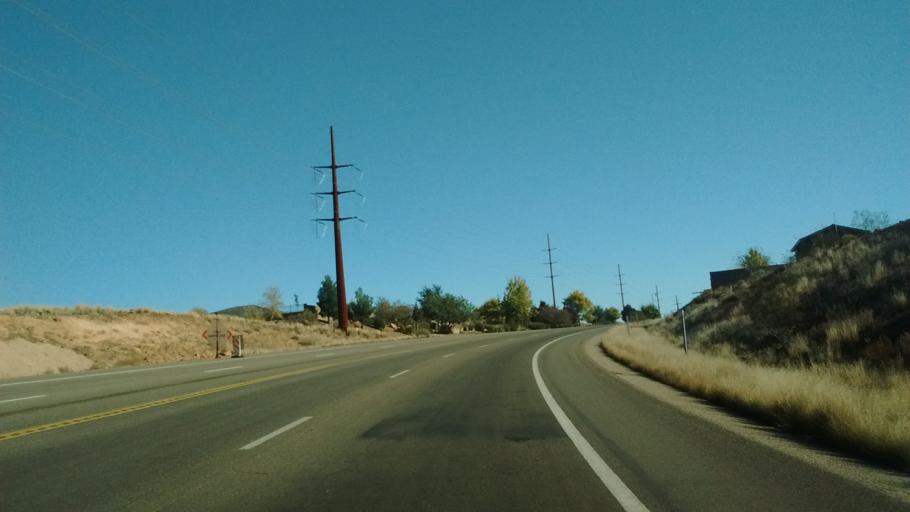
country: US
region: Utah
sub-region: Washington County
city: Washington
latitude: 37.1377
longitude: -113.4721
